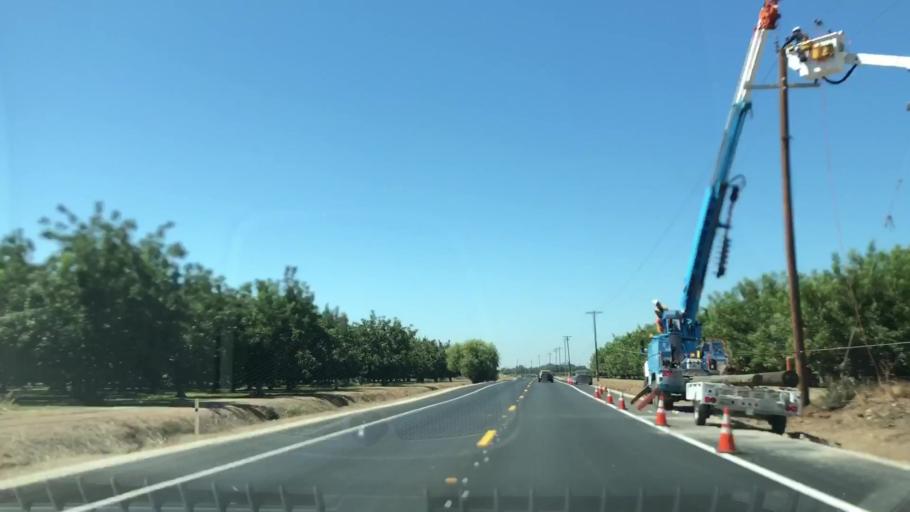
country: US
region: California
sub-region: San Joaquin County
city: Linden
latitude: 37.9341
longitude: -121.0658
